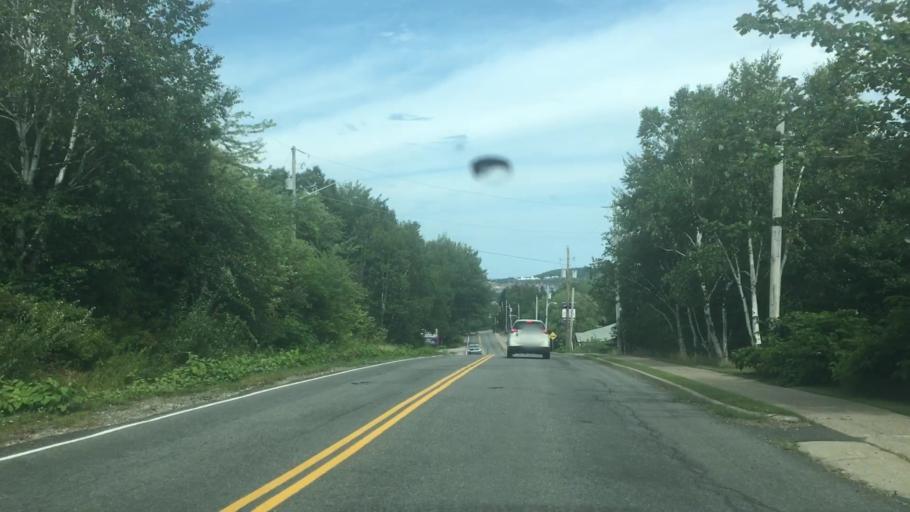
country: CA
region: Nova Scotia
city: Sydney Mines
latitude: 46.6371
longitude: -60.4111
